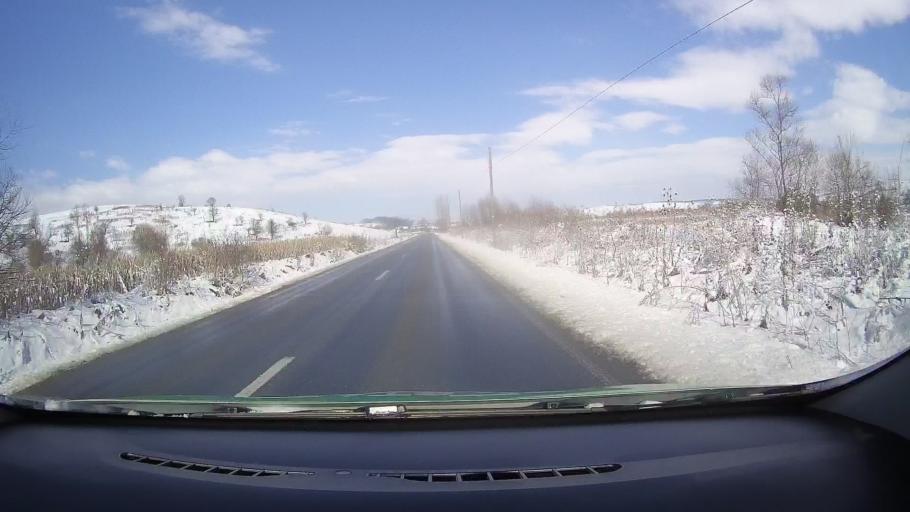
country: RO
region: Sibiu
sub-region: Comuna Nocrich
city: Nocrich
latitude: 45.8793
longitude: 24.4518
